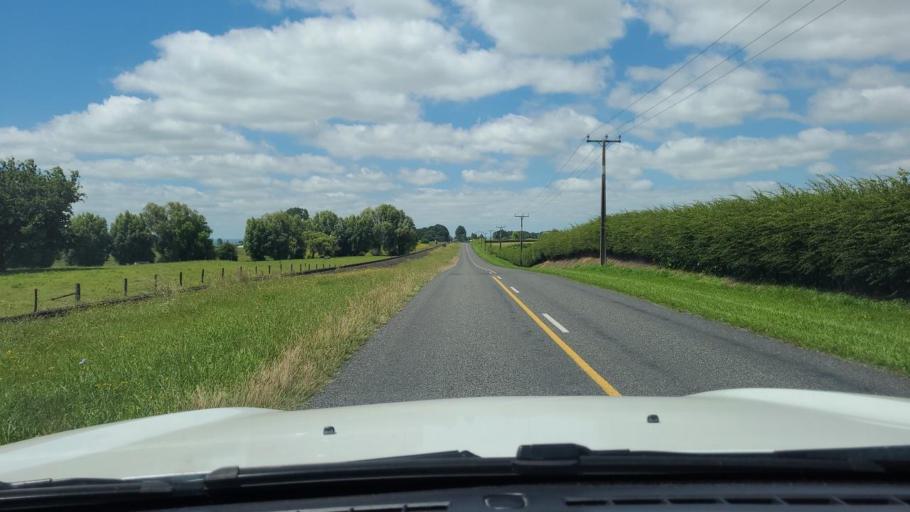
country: NZ
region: Waikato
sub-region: Matamata-Piako District
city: Matamata
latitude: -37.8695
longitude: 175.7561
